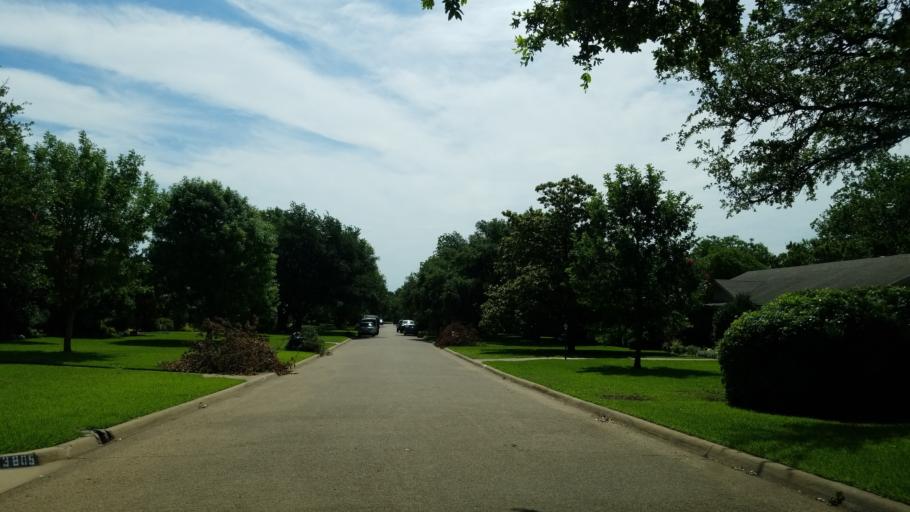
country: US
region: Texas
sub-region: Dallas County
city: Farmers Branch
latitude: 32.9061
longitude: -96.8511
